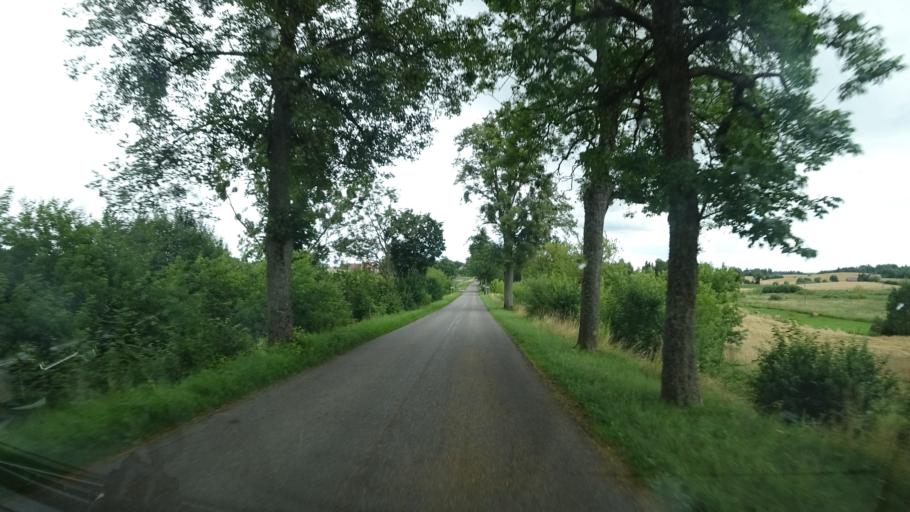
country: PL
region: Warmian-Masurian Voivodeship
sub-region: Powiat goldapski
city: Goldap
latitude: 54.3062
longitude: 22.4176
